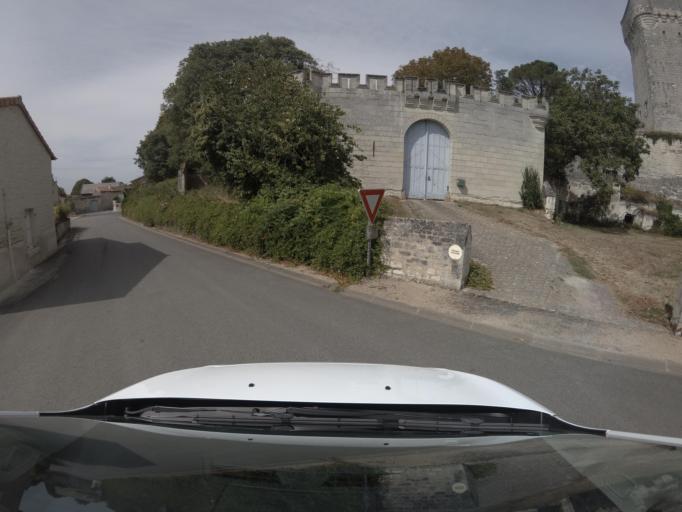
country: FR
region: Poitou-Charentes
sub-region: Departement des Deux-Sevres
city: Saint-Leger-de-Montbrun
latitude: 47.0125
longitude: -0.0567
